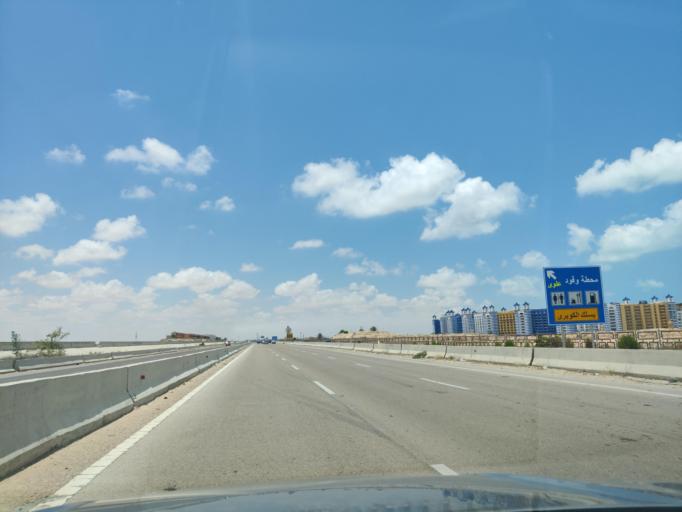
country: EG
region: Muhafazat Matruh
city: Al `Alamayn
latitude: 30.8212
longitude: 29.0108
